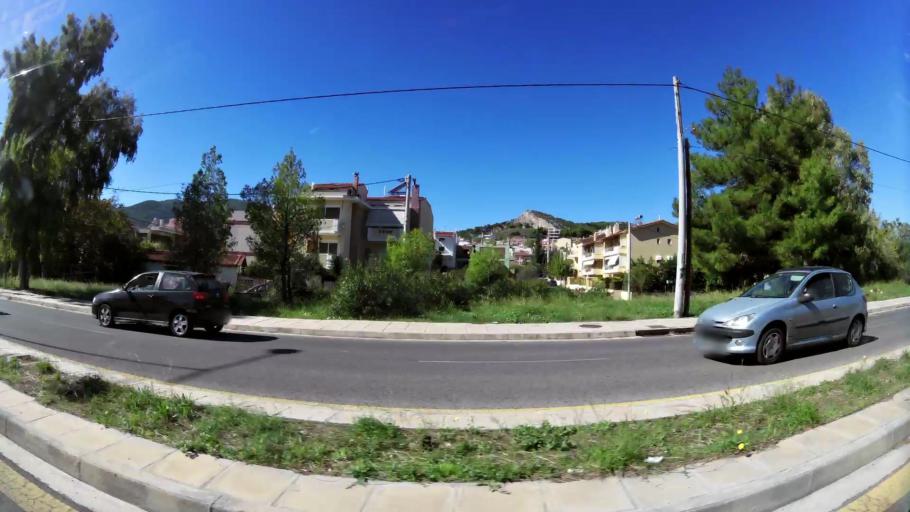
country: GR
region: Attica
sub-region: Nomarchia Anatolikis Attikis
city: Leondarion
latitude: 38.0023
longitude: 23.8547
